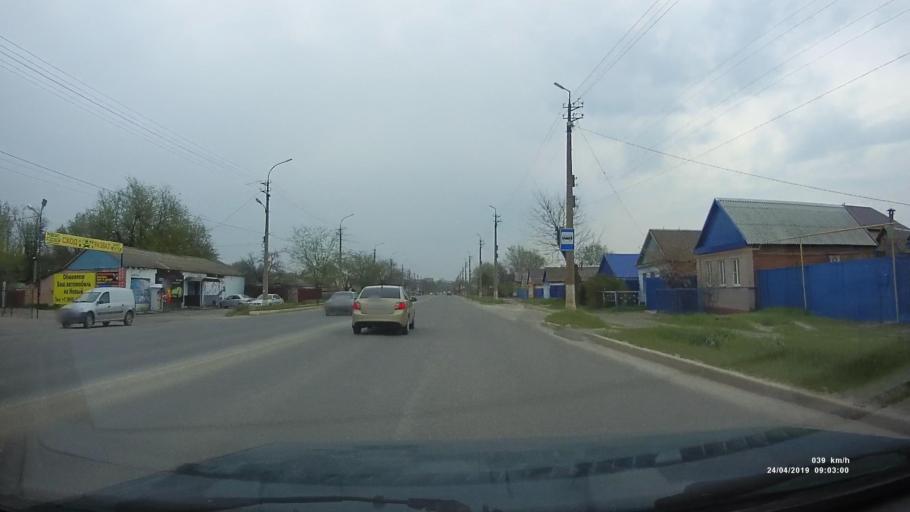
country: RU
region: Kalmykiya
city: Elista
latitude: 46.3118
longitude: 44.2342
